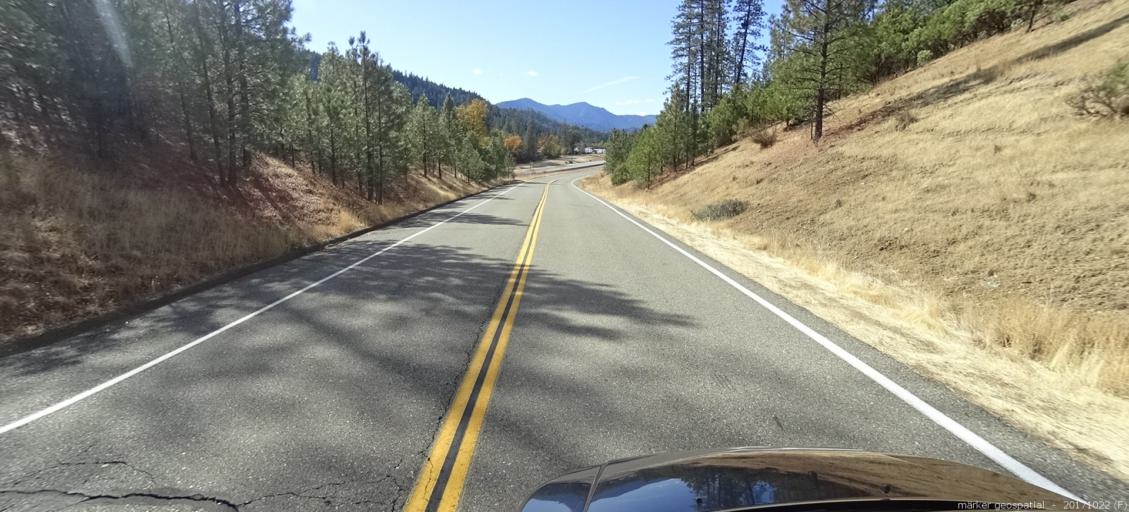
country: US
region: California
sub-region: Siskiyou County
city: Dunsmuir
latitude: 40.9989
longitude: -122.4170
